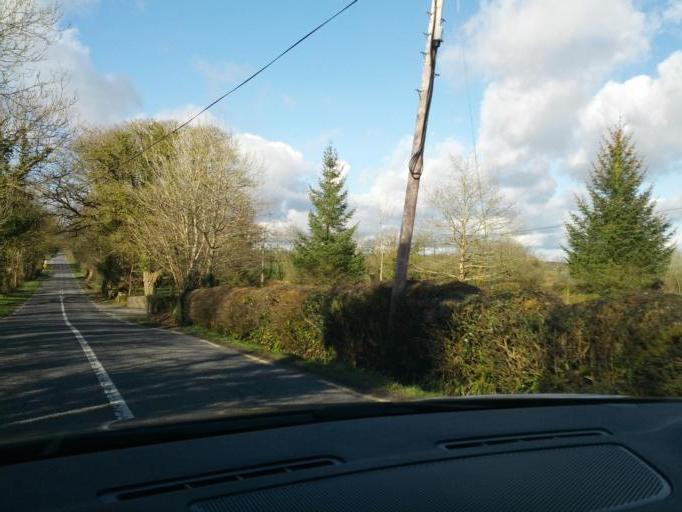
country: IE
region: Connaught
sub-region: Roscommon
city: Castlerea
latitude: 53.5372
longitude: -8.5551
